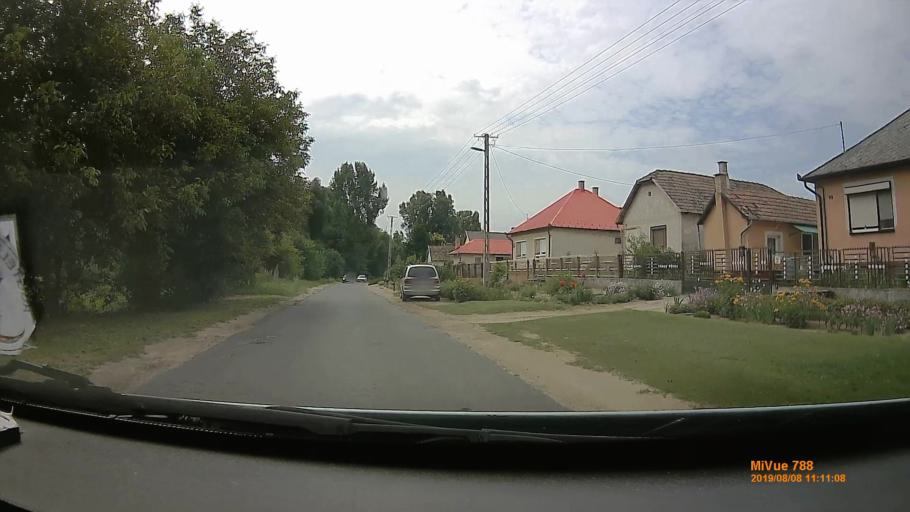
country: HU
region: Szabolcs-Szatmar-Bereg
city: Balkany
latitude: 47.7420
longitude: 21.8389
